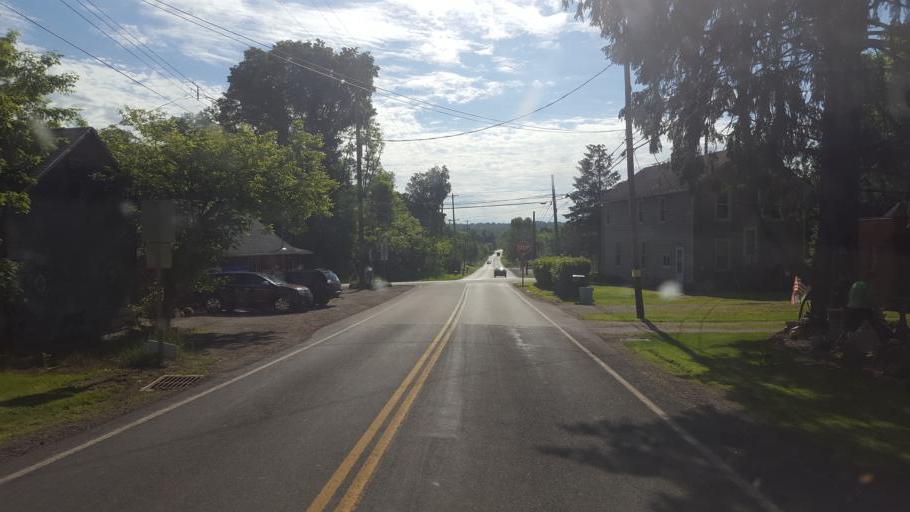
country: US
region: Ohio
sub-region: Medina County
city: Wadsworth
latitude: 41.0571
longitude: -81.8006
